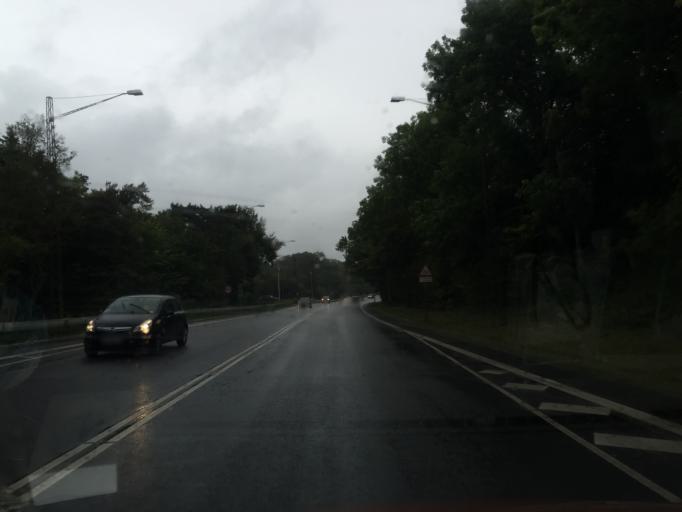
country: DK
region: South Denmark
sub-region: Fredericia Kommune
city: Snoghoj
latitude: 55.5083
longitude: 9.7024
